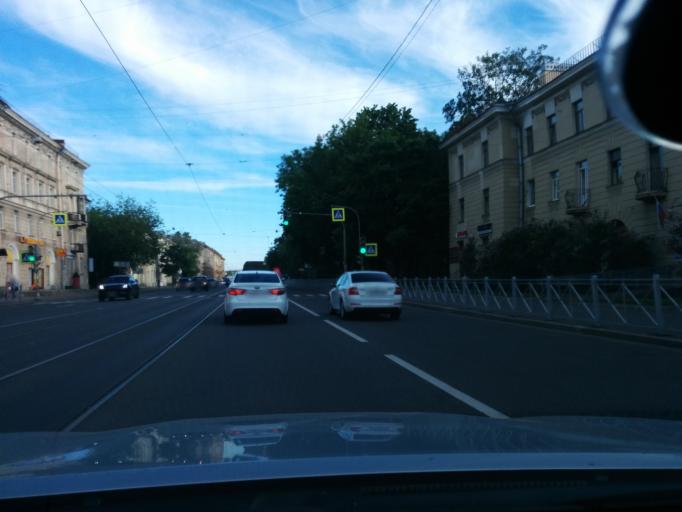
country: RU
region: Leningrad
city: Udel'naya
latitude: 60.0154
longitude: 30.3228
